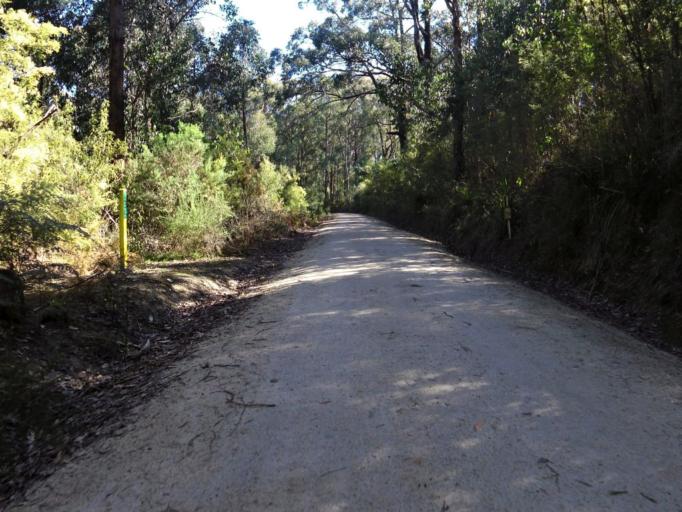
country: AU
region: Victoria
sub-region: Latrobe
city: Moe
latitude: -38.3902
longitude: 146.1832
